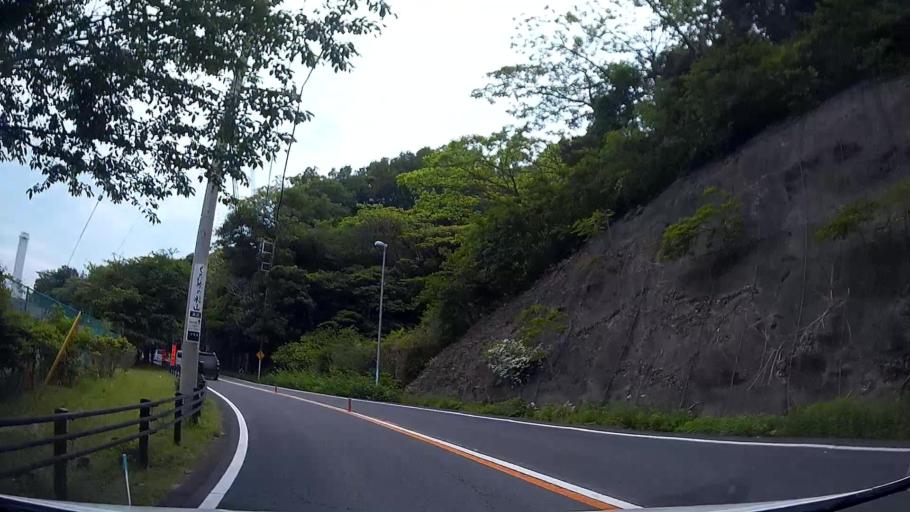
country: JP
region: Shizuoka
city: Ito
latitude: 35.0270
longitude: 139.0957
